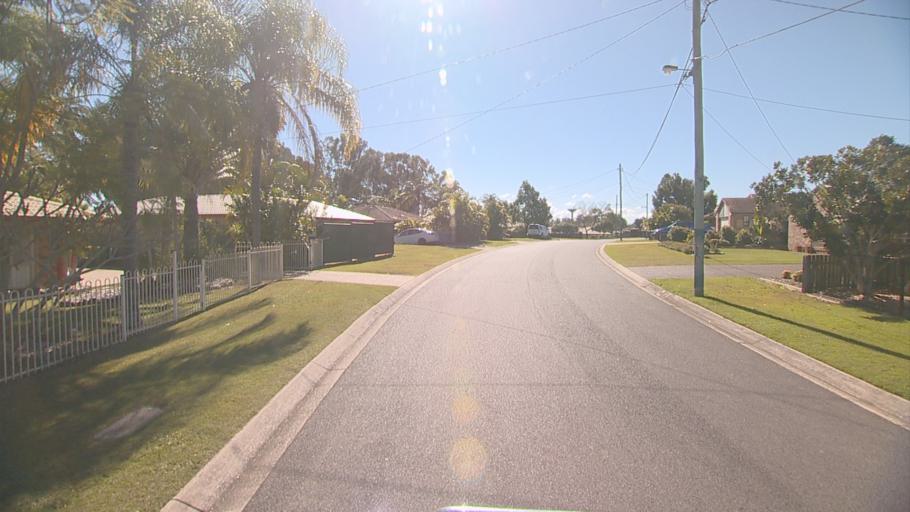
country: AU
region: Queensland
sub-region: Logan
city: Park Ridge South
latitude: -27.6865
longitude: 153.0288
